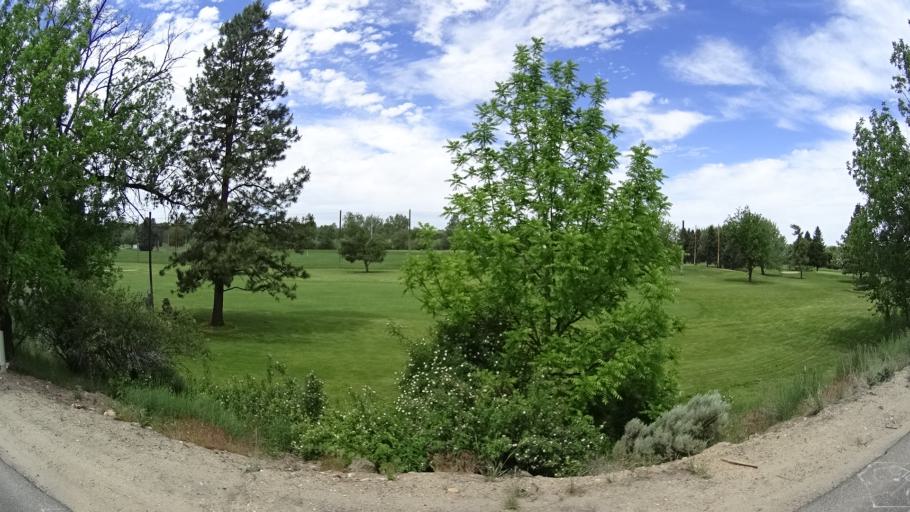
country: US
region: Idaho
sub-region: Ada County
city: Boise
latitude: 43.5941
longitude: -116.1633
